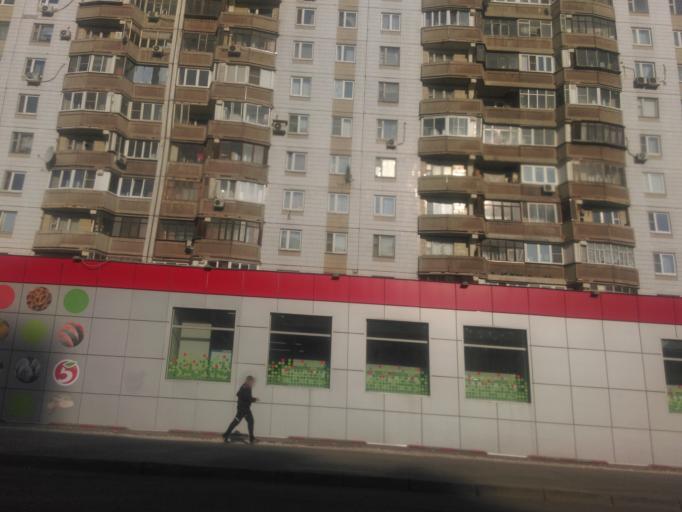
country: RU
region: Moscow
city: Novo-Peredelkino
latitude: 55.6397
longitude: 37.3541
